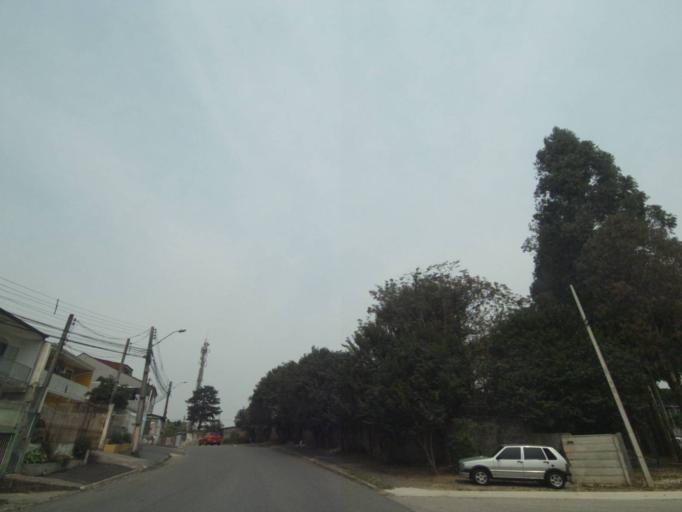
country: BR
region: Parana
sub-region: Sao Jose Dos Pinhais
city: Sao Jose dos Pinhais
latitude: -25.5197
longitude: -49.2899
